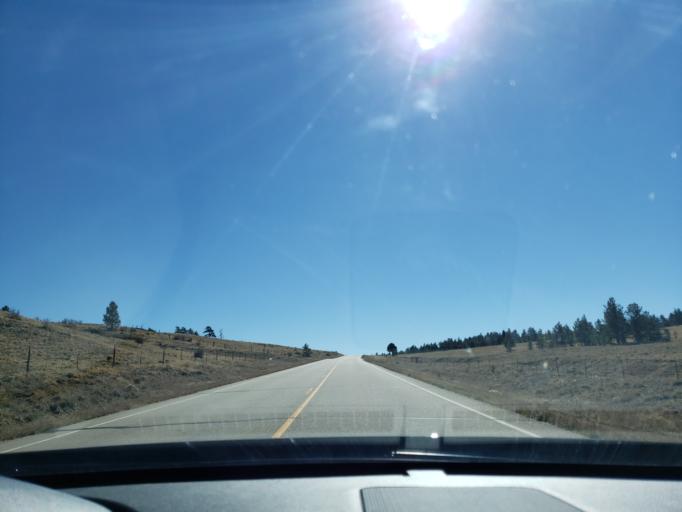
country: US
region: Colorado
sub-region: Park County
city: Fairplay
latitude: 38.9132
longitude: -105.7032
